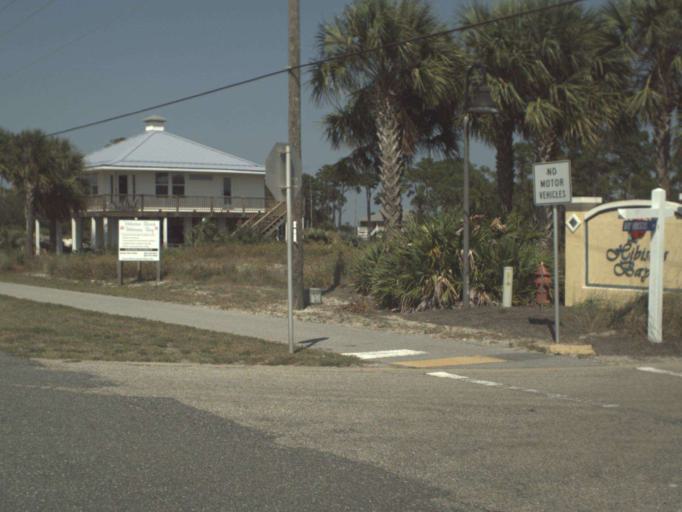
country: US
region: Florida
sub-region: Gulf County
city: Port Saint Joe
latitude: 29.7231
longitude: -85.3873
